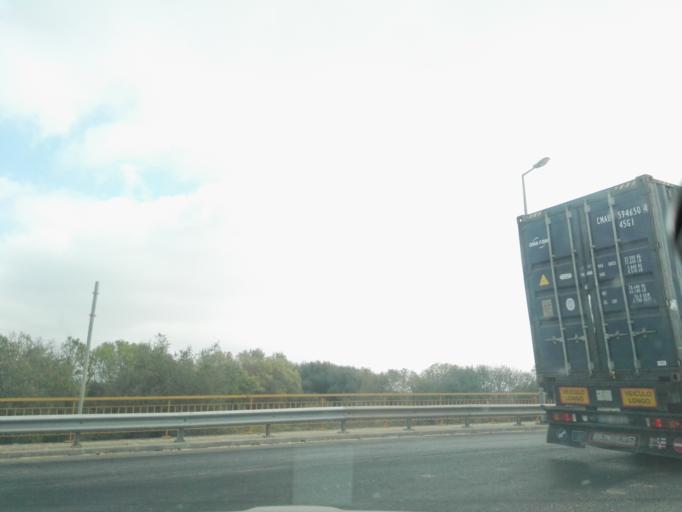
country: PT
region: Santarem
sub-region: Benavente
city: Benavente
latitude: 38.9896
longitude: -8.8100
